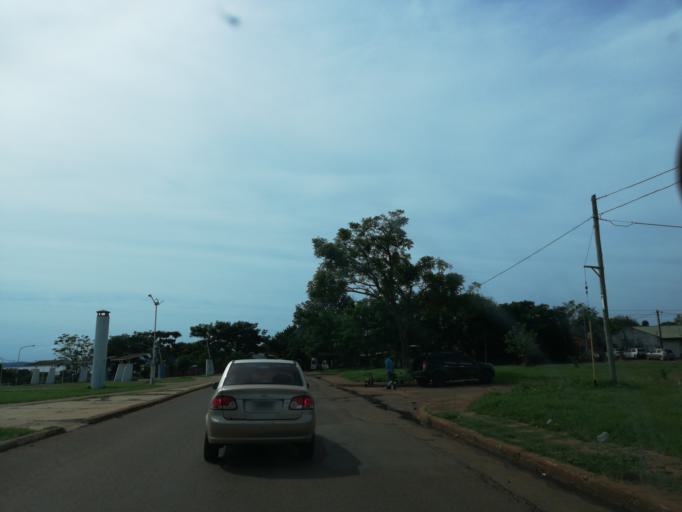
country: AR
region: Misiones
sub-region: Departamento de Capital
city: Posadas
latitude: -27.4286
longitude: -55.8792
